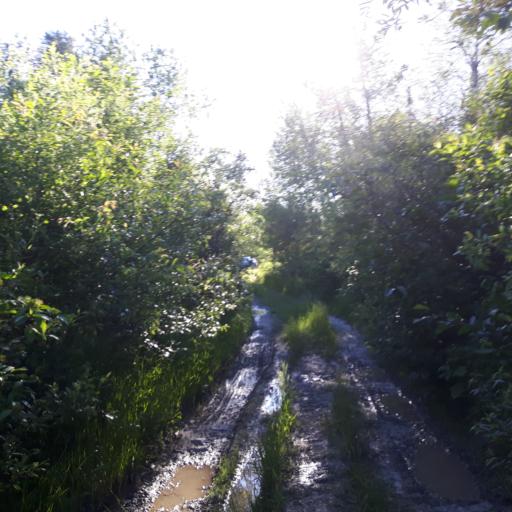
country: CA
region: Ontario
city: Red Lake
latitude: 50.9796
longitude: -93.8708
